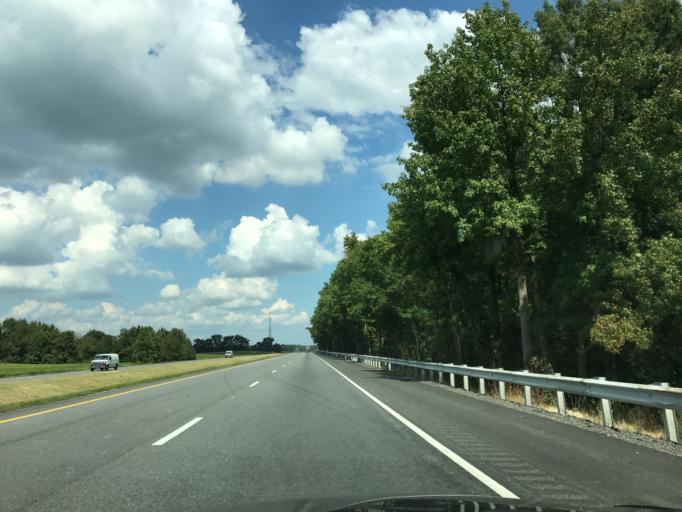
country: US
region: Maryland
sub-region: Queen Anne's County
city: Kingstown
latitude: 39.1614
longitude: -75.9199
